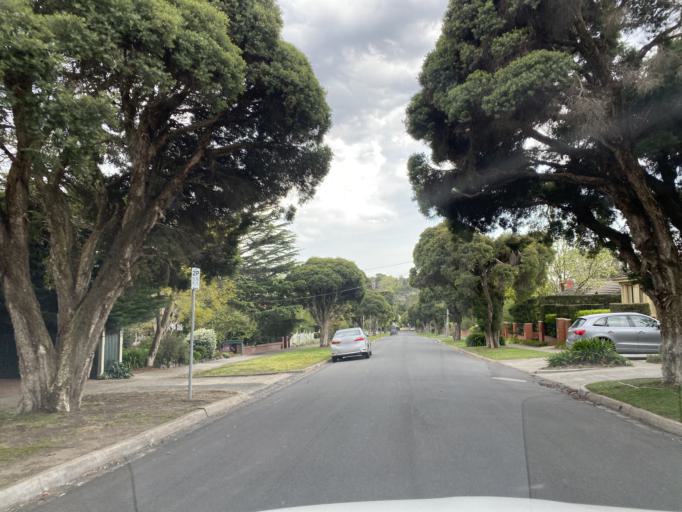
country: AU
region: Victoria
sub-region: Boroondara
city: Canterbury
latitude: -37.8280
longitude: 145.0787
